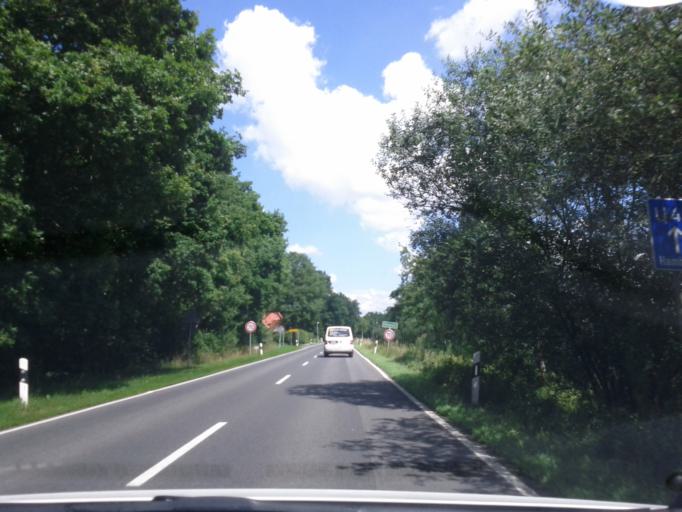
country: DE
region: Lower Saxony
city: Wohnste
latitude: 53.3317
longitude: 9.5318
